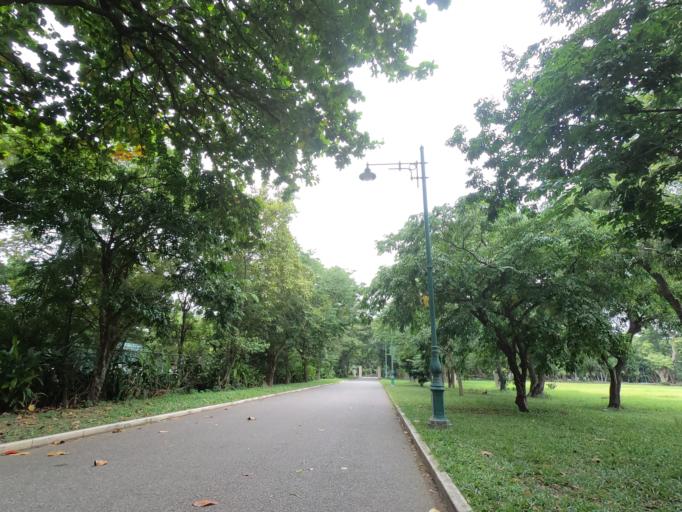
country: TH
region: Nakhon Pathom
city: Nakhon Pathom
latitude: 13.8201
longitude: 100.0477
